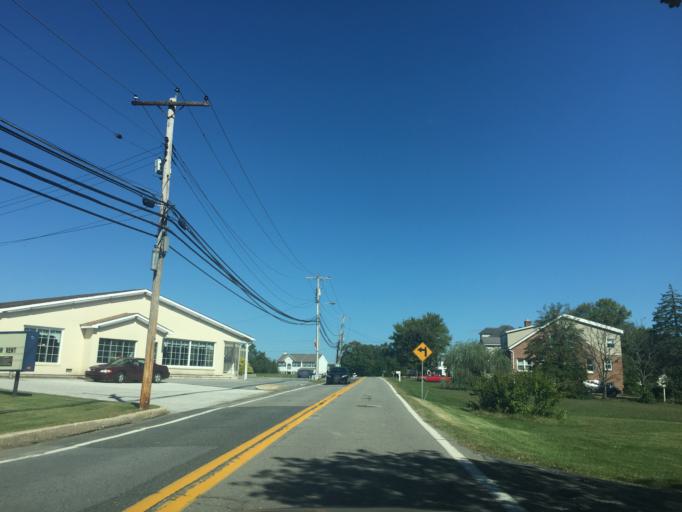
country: US
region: Maryland
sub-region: Baltimore County
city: Rossville
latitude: 39.3618
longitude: -76.4912
